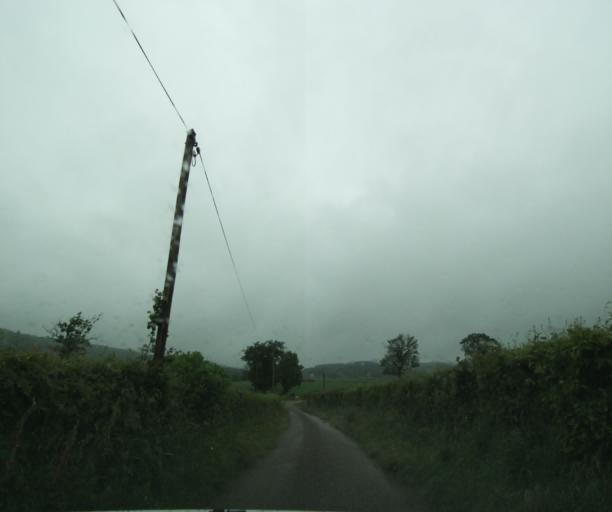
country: FR
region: Bourgogne
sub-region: Departement de Saone-et-Loire
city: La Clayette
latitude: 46.3683
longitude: 4.3777
